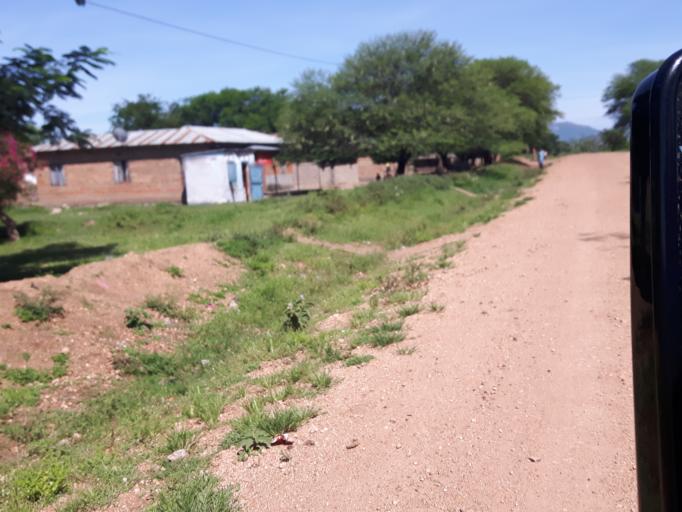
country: TZ
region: Mara
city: Issenye
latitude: -1.9610
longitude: 34.2707
